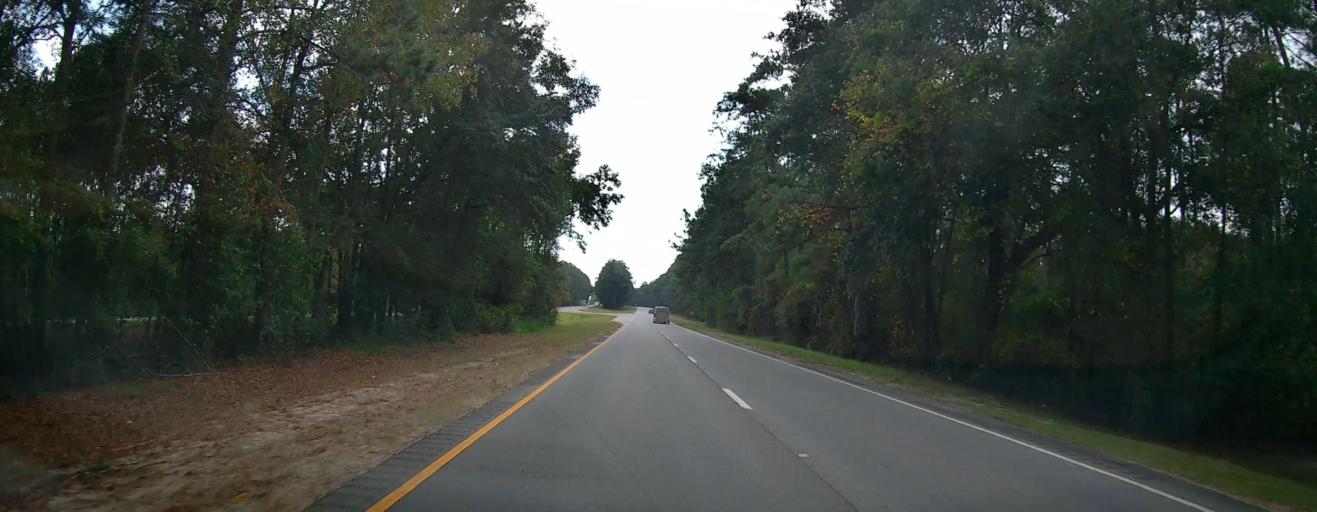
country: US
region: Georgia
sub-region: Thomas County
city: Thomasville
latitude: 30.7664
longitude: -84.0843
